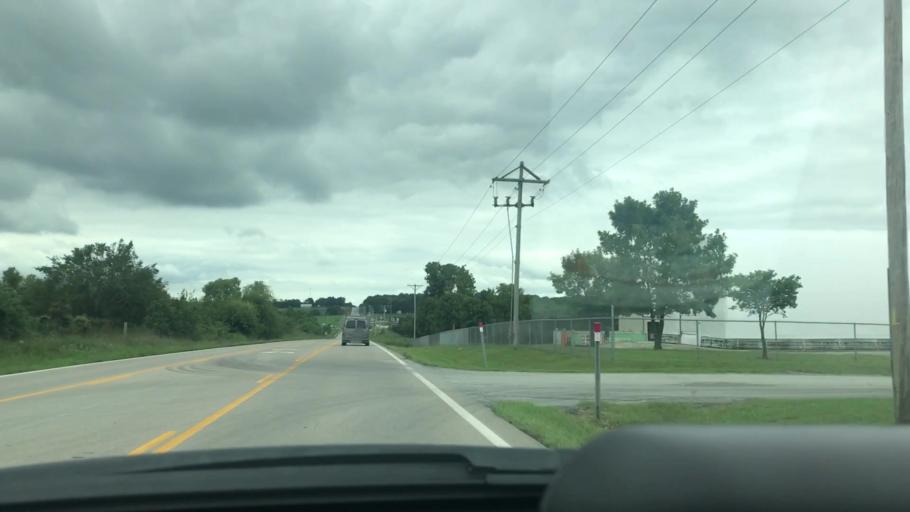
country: US
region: Missouri
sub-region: Dallas County
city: Buffalo
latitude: 37.6603
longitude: -93.1035
